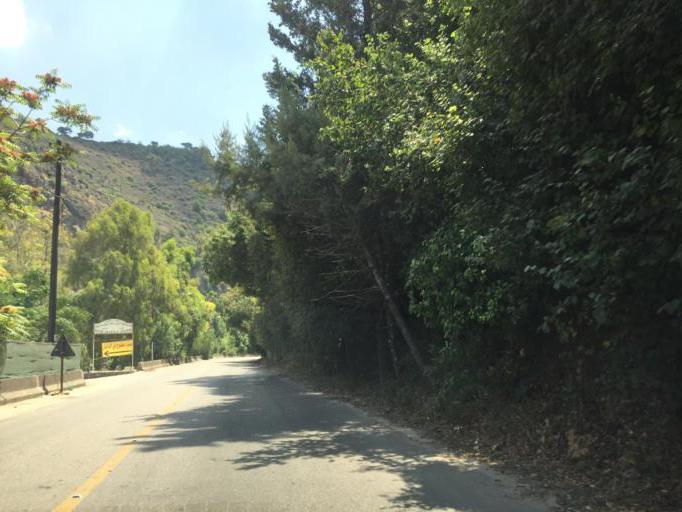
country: LB
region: Mont-Liban
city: Beit ed Dine
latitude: 33.7008
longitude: 35.4698
